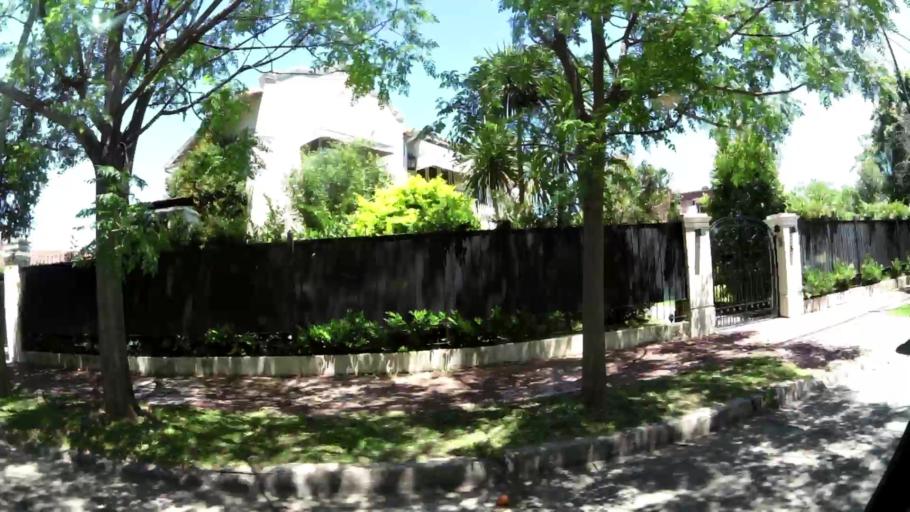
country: AR
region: Buenos Aires
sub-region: Partido de San Isidro
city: San Isidro
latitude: -34.4761
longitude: -58.5015
